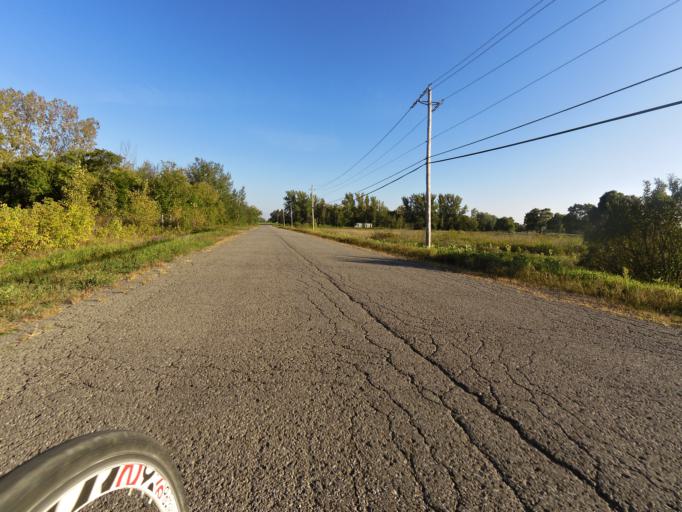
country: CA
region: Ontario
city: Bells Corners
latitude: 45.2169
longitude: -75.7144
